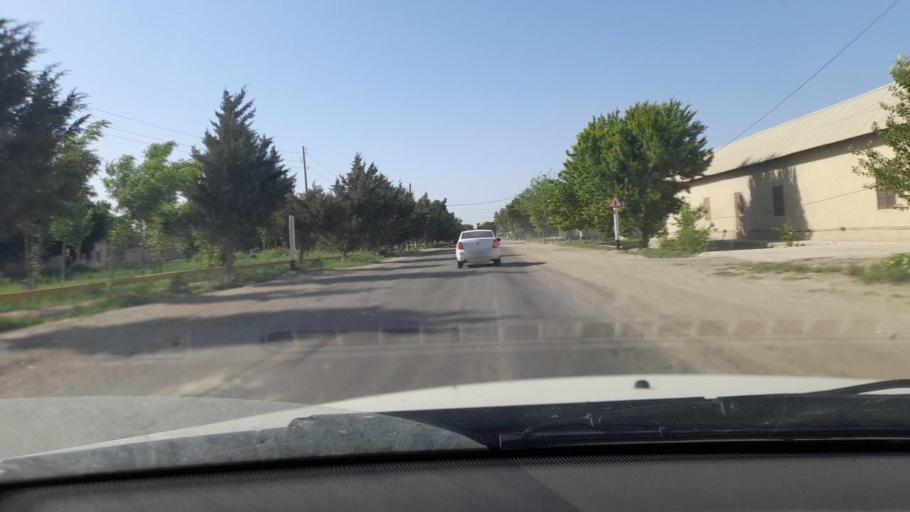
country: UZ
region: Bukhara
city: Romiton
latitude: 40.0628
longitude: 64.3270
